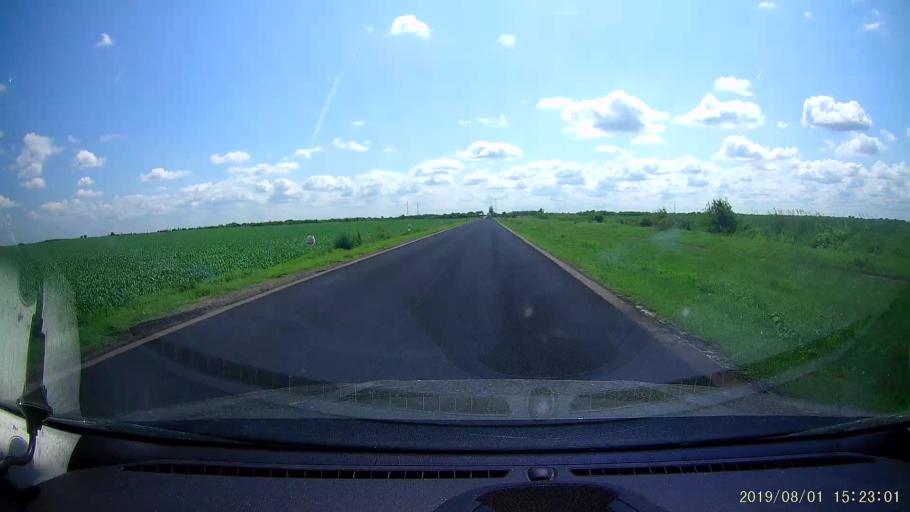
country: RO
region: Braila
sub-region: Comuna Viziru
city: Lanurile
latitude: 45.0459
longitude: 27.7664
